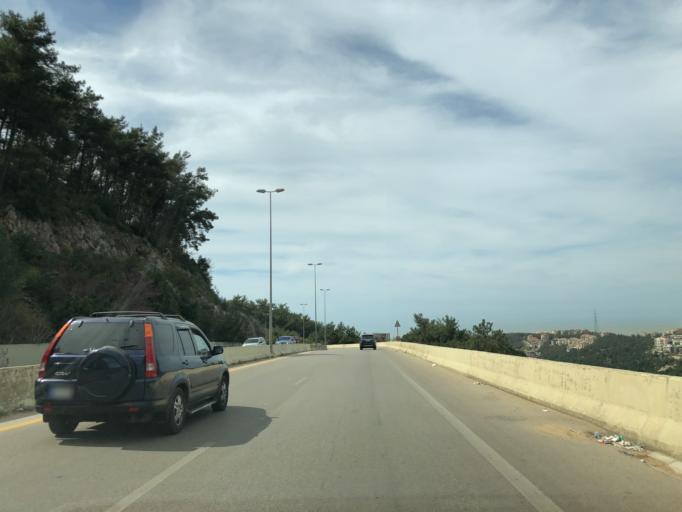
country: LB
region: Mont-Liban
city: Jdaidet el Matn
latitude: 33.9003
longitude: 35.6439
